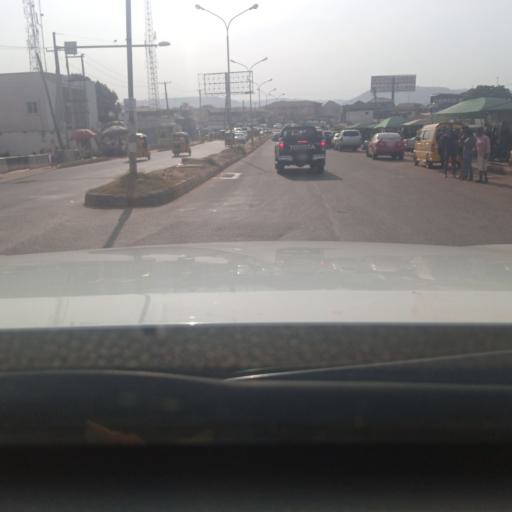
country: NG
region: Enugu
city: Enugu
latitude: 6.4408
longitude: 7.5070
